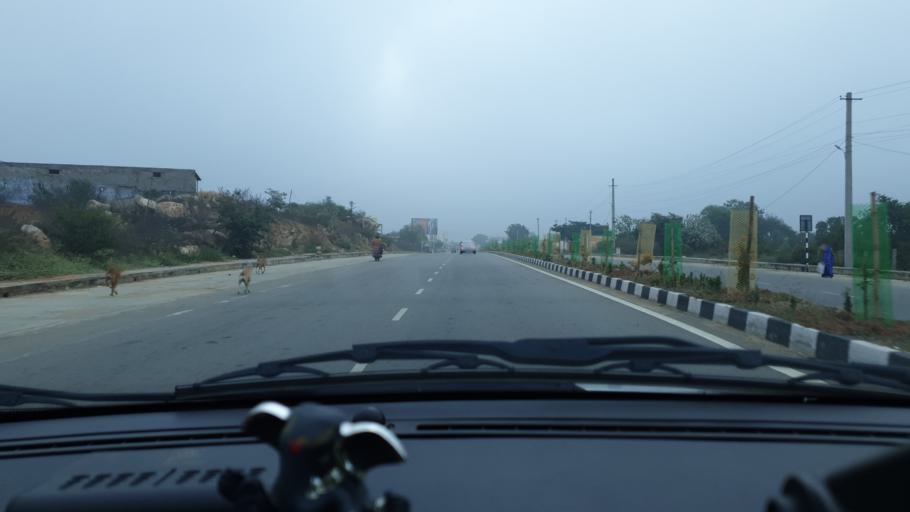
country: IN
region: Telangana
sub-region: Mahbubnagar
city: Farrukhnagar
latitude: 16.9537
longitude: 78.5182
